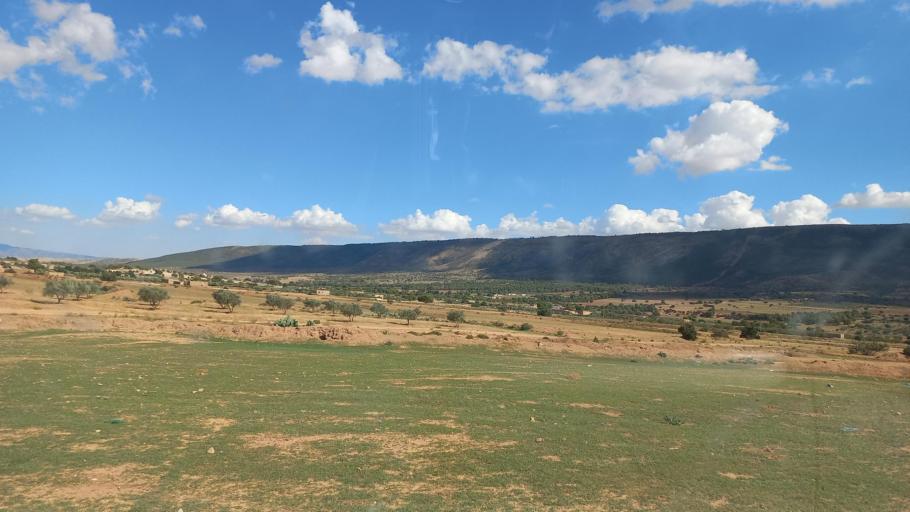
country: TN
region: Al Qasrayn
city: Kasserine
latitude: 35.3722
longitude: 8.8835
